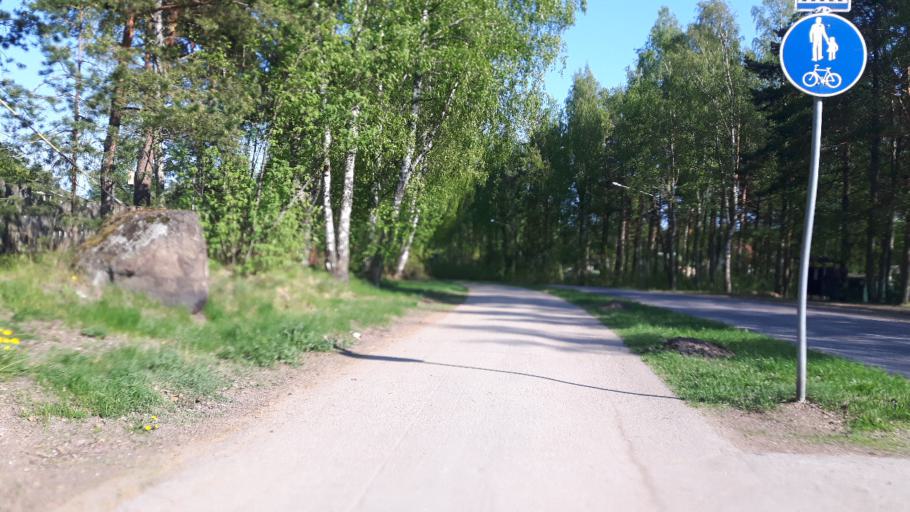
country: FI
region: Kymenlaakso
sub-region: Kotka-Hamina
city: Kotka
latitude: 60.4751
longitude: 26.8727
